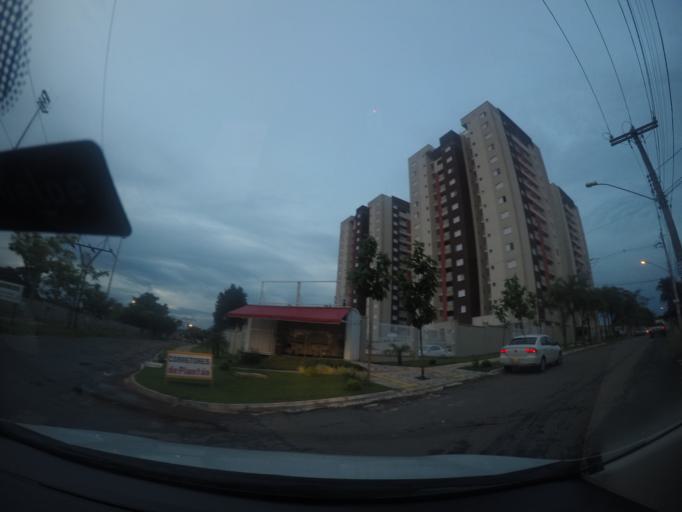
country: BR
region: Goias
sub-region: Goiania
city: Goiania
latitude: -16.6437
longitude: -49.2464
